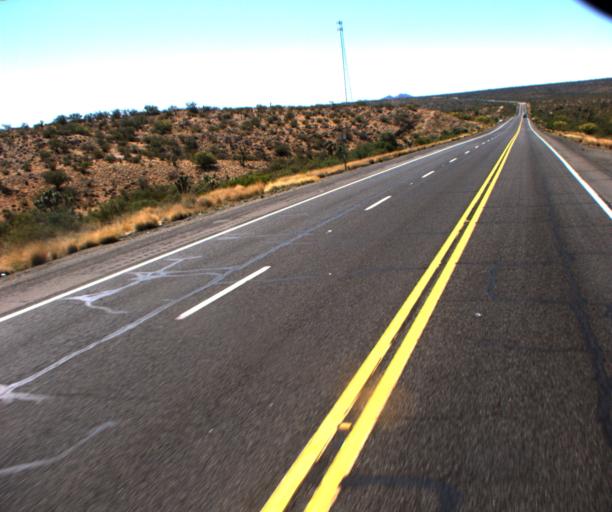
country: US
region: Arizona
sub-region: Yavapai County
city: Congress
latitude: 34.2190
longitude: -113.0682
